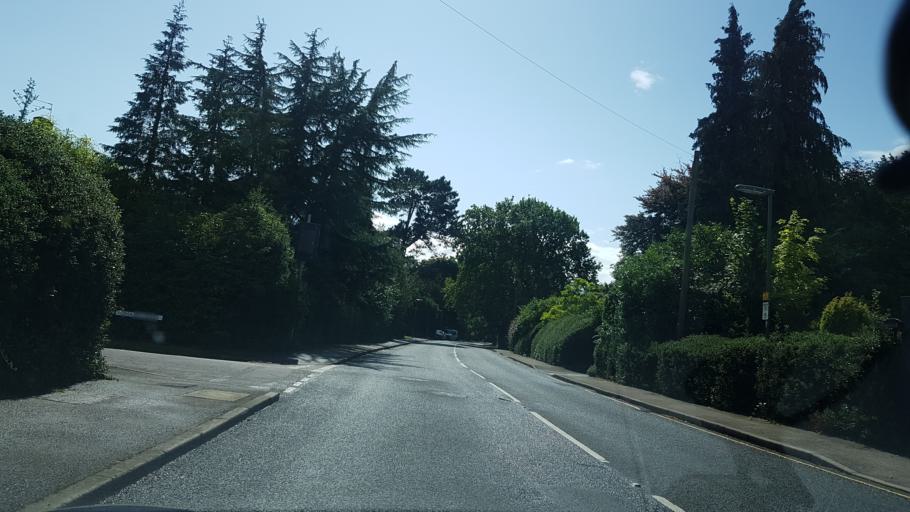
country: GB
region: England
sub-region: Surrey
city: West Byfleet
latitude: 51.3308
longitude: -0.5088
